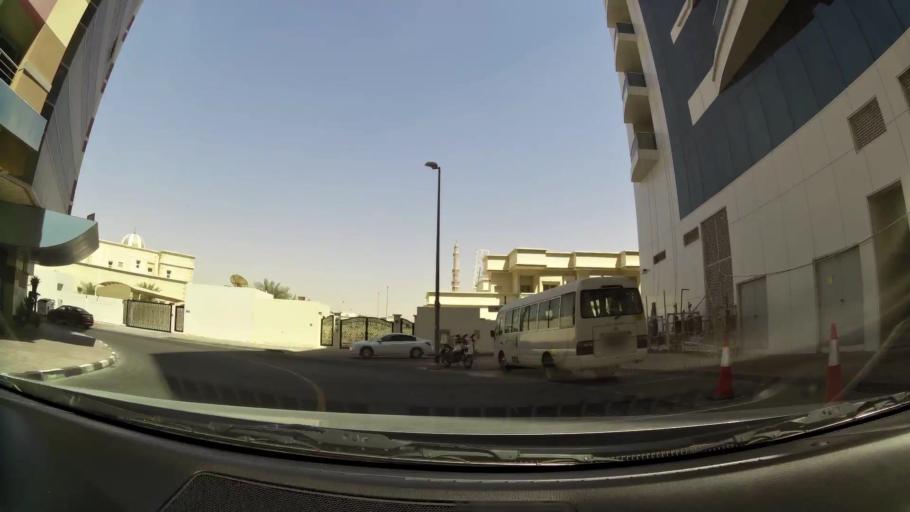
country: AE
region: Dubai
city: Dubai
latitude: 25.1091
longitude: 55.2041
